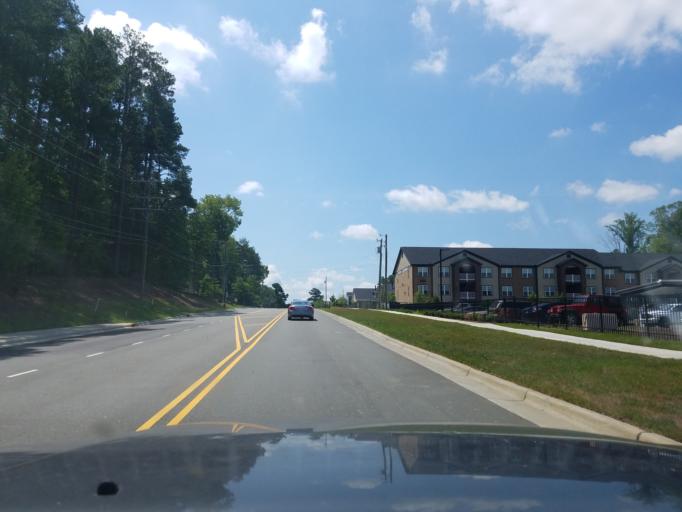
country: US
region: North Carolina
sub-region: Durham County
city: Durham
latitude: 35.9538
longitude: -78.9722
